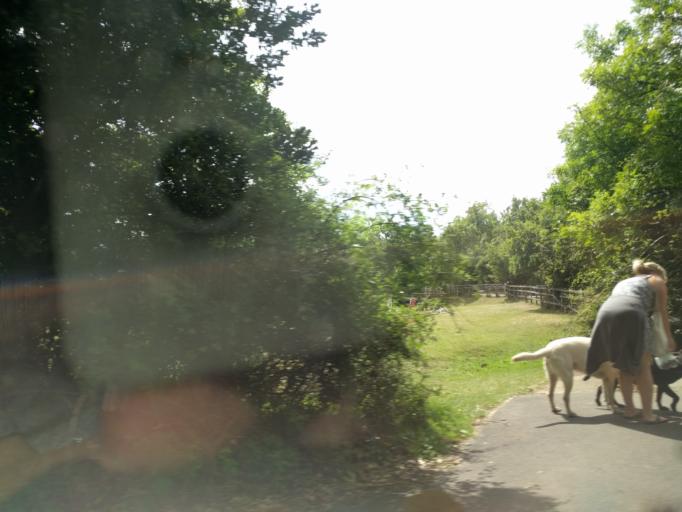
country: GB
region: England
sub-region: Hampshire
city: Brockenhurst
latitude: 50.8271
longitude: -1.5711
